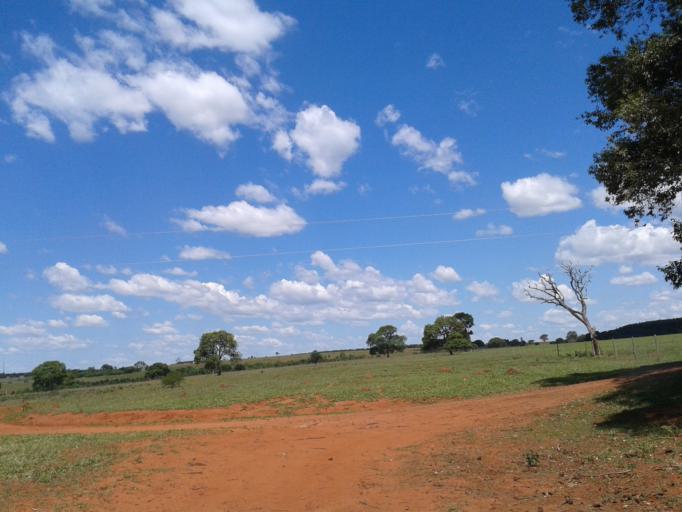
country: BR
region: Minas Gerais
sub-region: Centralina
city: Centralina
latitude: -18.7200
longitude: -49.1571
